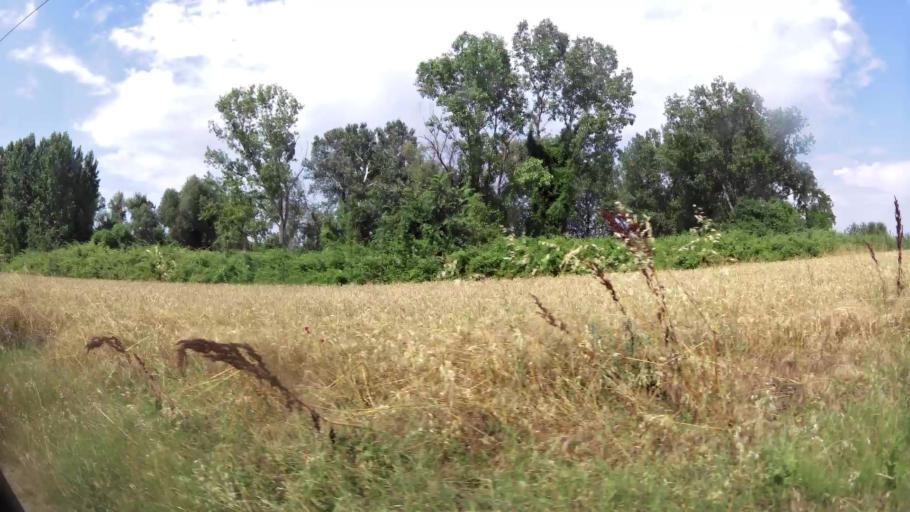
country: GR
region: Central Macedonia
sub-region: Nomos Pierias
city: Makrygialos
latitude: 40.3823
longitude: 22.6204
